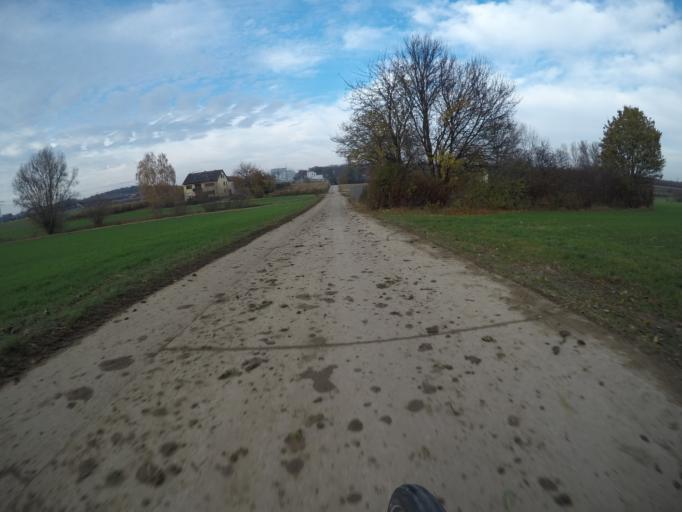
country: DE
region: Baden-Wuerttemberg
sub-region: Regierungsbezirk Stuttgart
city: Leinfelden-Echterdingen
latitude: 48.7010
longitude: 9.1733
